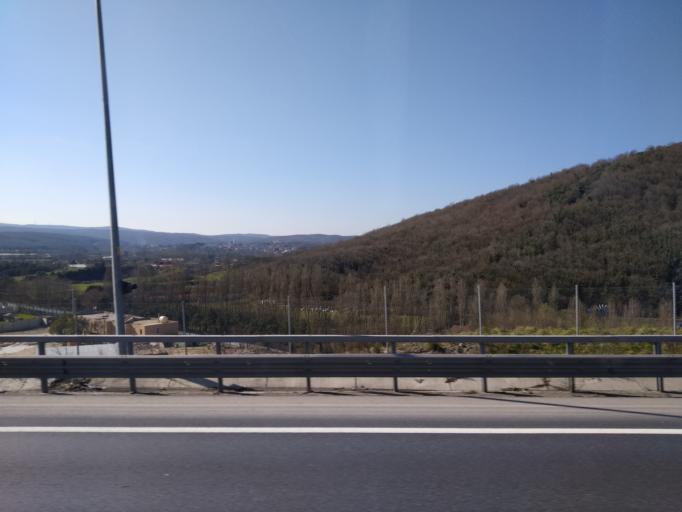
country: TR
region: Istanbul
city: Mahmut Sevket Pasa
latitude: 41.1357
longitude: 29.2867
